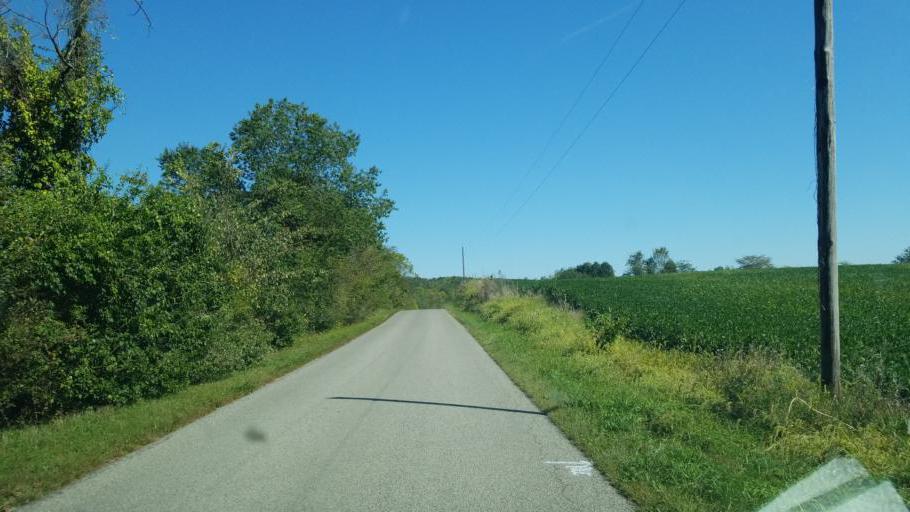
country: US
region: Ohio
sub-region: Logan County
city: West Liberty
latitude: 40.3051
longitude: -83.7266
